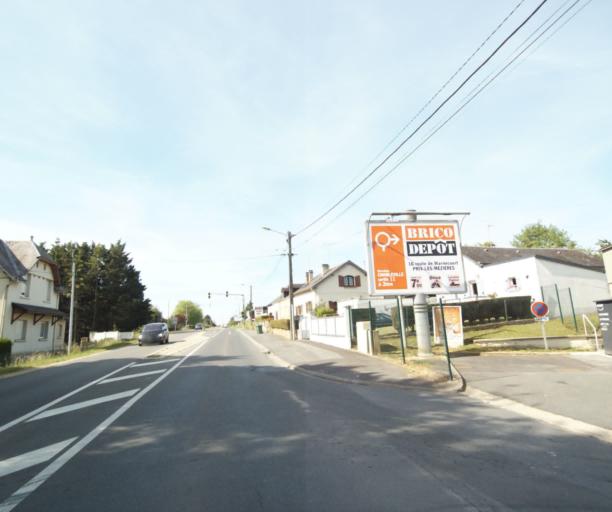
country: FR
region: Champagne-Ardenne
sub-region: Departement des Ardennes
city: La Francheville
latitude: 49.7398
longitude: 4.7248
